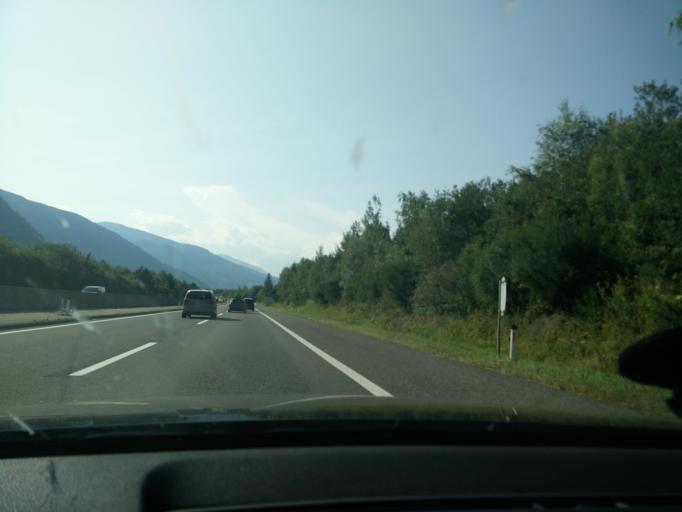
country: AT
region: Carinthia
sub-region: Villach Stadt
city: Villach
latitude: 46.6437
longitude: 13.8847
